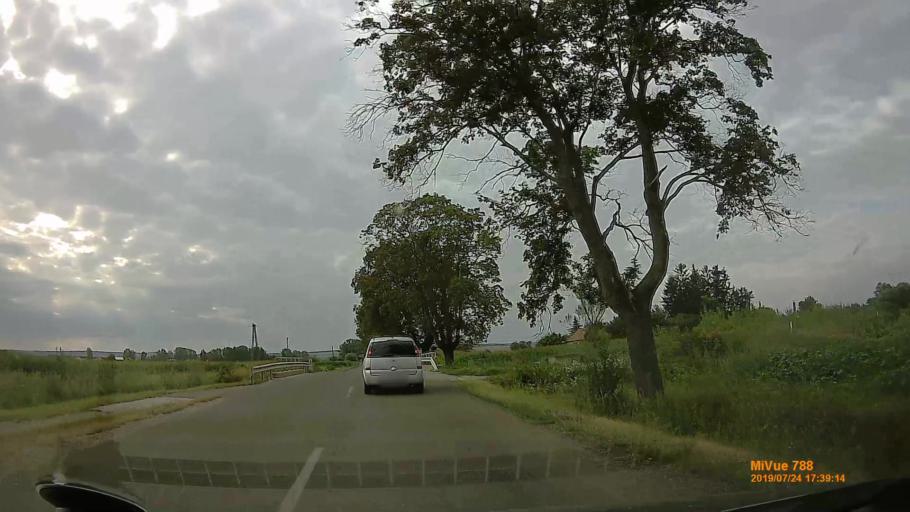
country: HU
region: Borsod-Abauj-Zemplen
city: Encs
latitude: 48.3250
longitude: 21.1472
